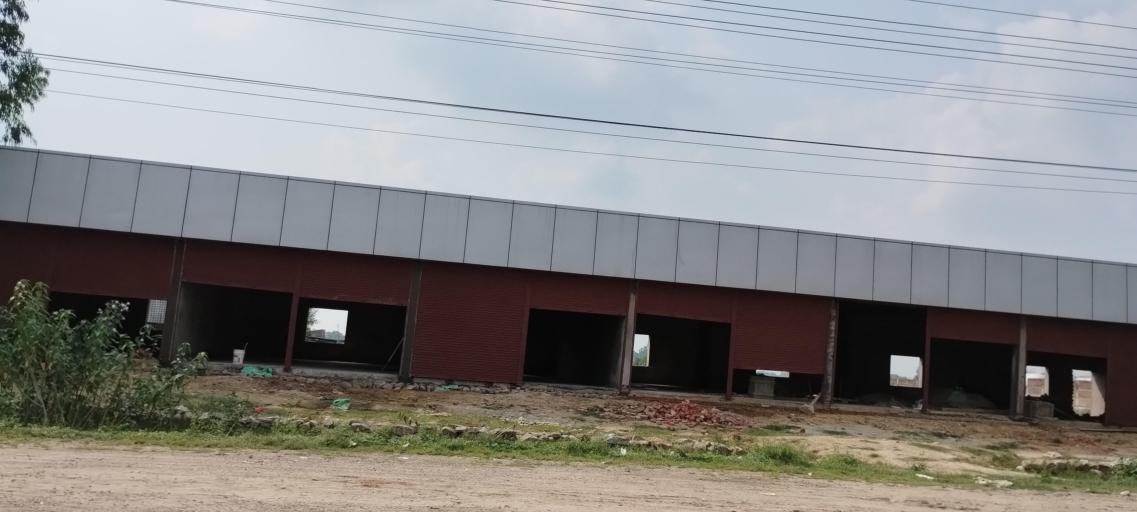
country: NP
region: Mid Western
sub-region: Bheri Zone
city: Nepalgunj
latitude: 28.1561
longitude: 81.6692
